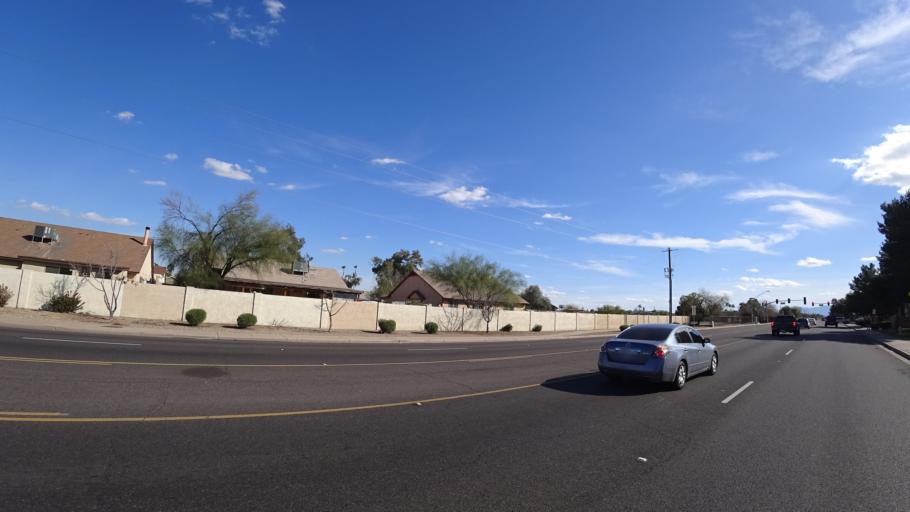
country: US
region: Arizona
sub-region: Maricopa County
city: Glendale
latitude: 33.5320
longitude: -112.2206
